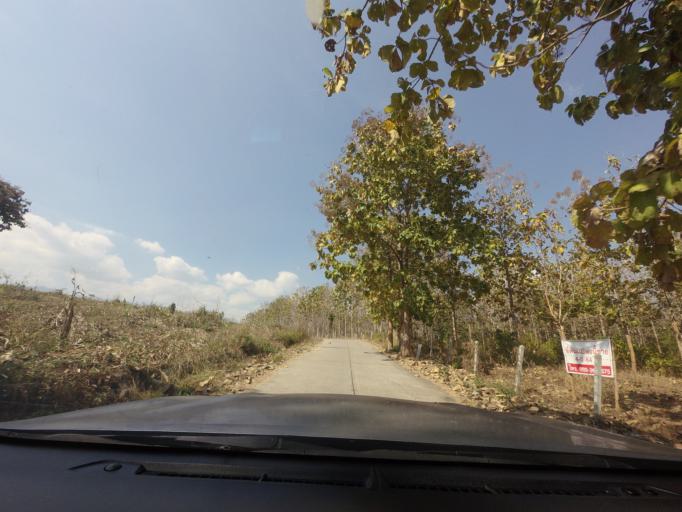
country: TH
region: Mae Hong Son
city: Wiang Nuea
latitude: 19.3839
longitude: 98.4359
